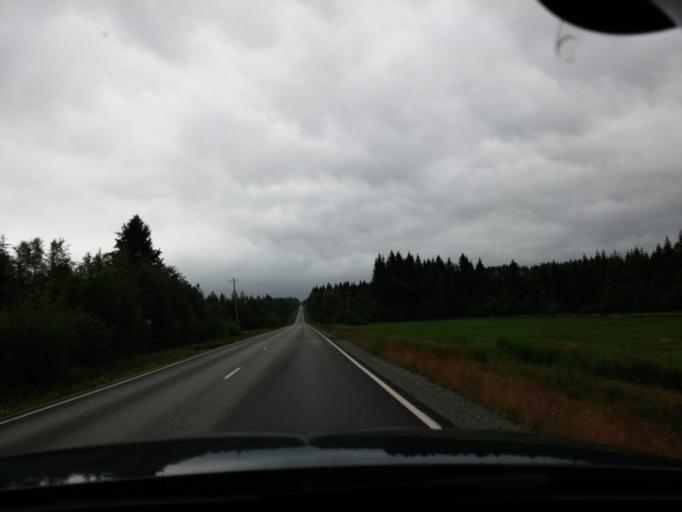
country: FI
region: Central Finland
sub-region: Saarijaervi-Viitasaari
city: Pylkoenmaeki
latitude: 62.6411
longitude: 24.8804
